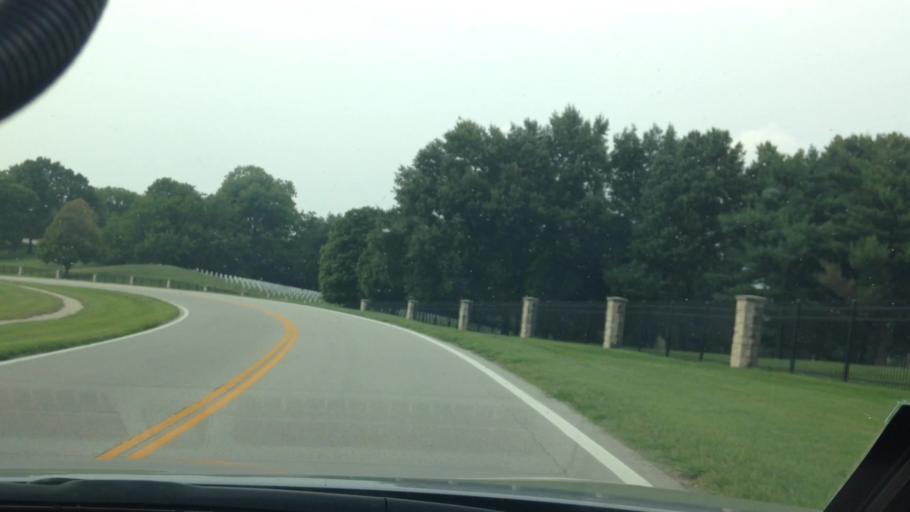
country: US
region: Kansas
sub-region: Leavenworth County
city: Lansing
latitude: 39.2733
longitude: -94.8905
